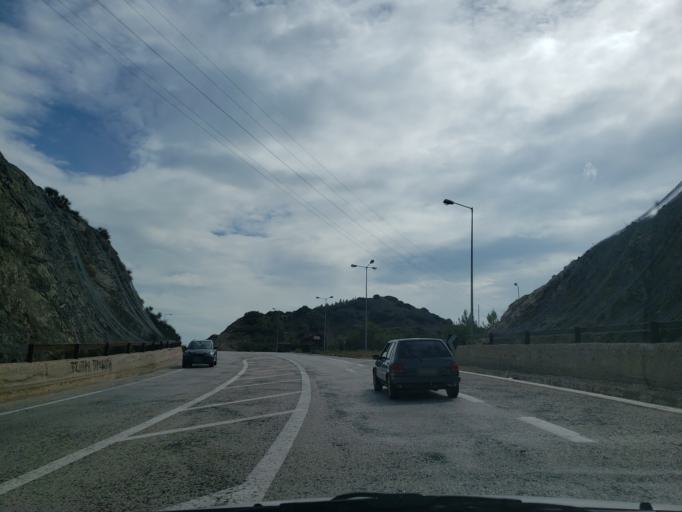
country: GR
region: Central Greece
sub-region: Nomos Fthiotidos
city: Stavros
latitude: 38.9893
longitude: 22.3731
